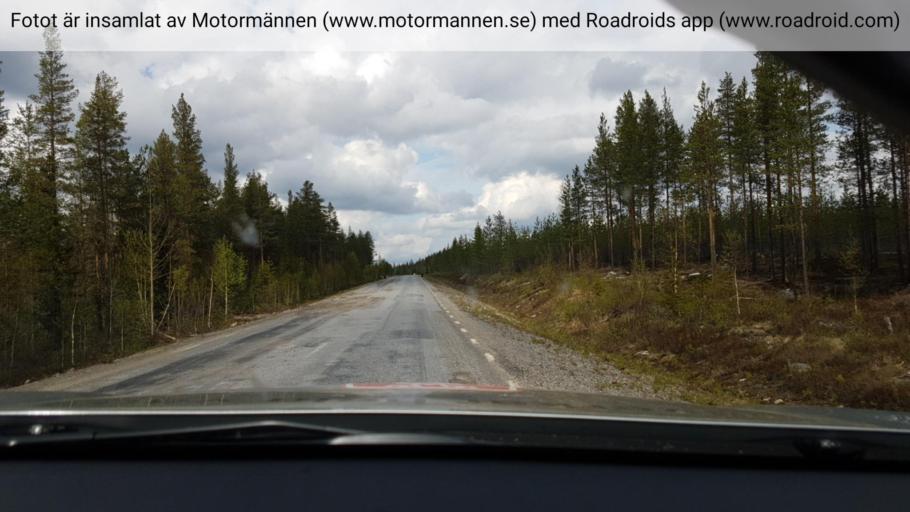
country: SE
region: Vaesterbotten
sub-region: Lycksele Kommun
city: Lycksele
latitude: 63.9696
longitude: 18.4979
